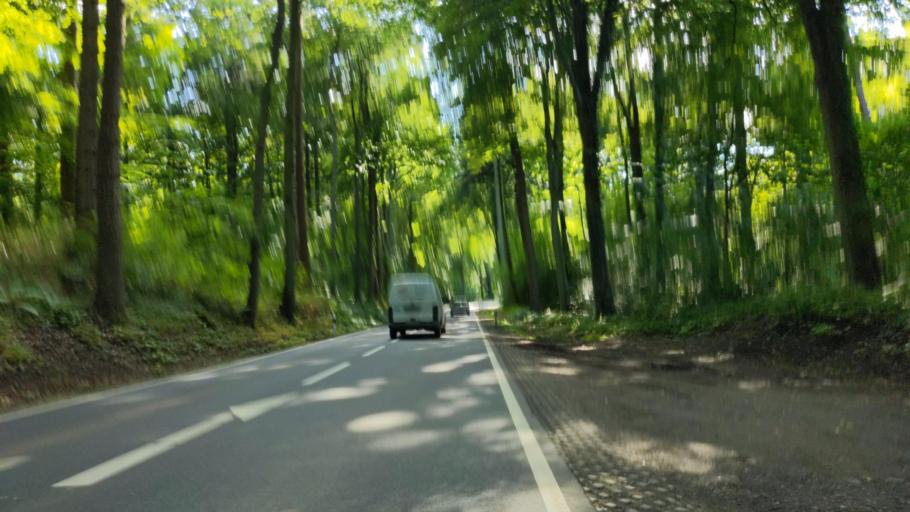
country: DE
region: Schleswig-Holstein
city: Kasseedorf
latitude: 54.1511
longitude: 10.7124
